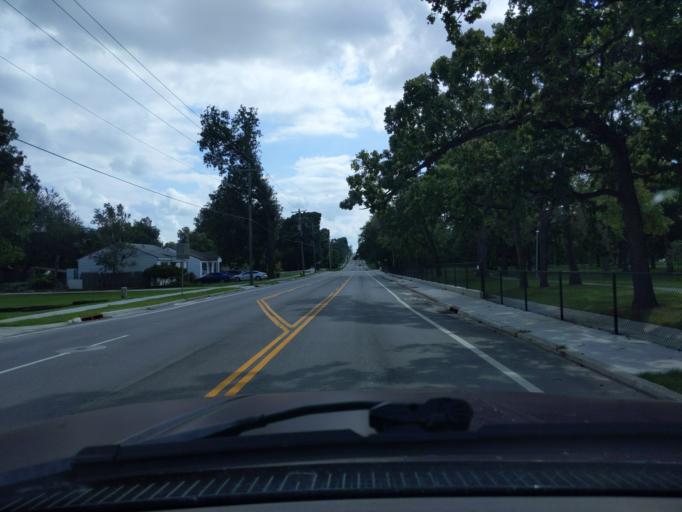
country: US
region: Oklahoma
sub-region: Tulsa County
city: Tulsa
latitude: 36.1038
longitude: -96.0116
